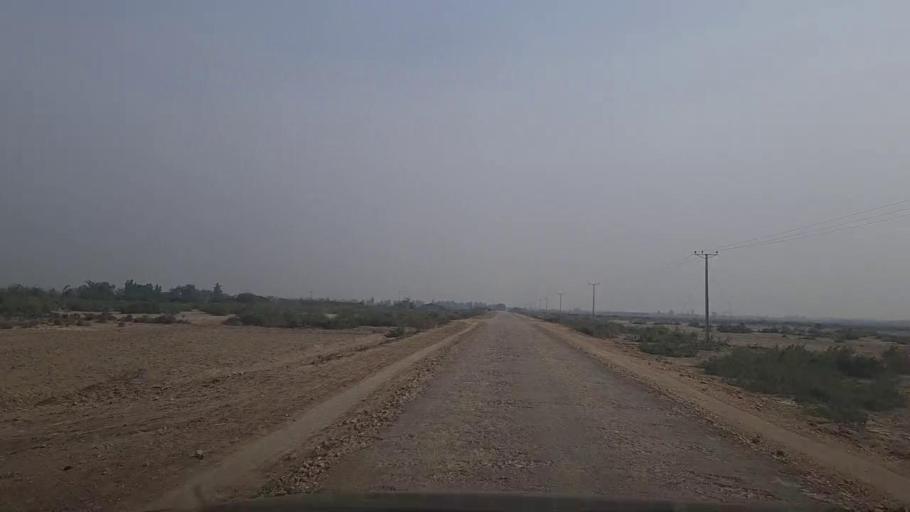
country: PK
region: Sindh
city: Mirpur Sakro
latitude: 24.4588
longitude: 67.6981
